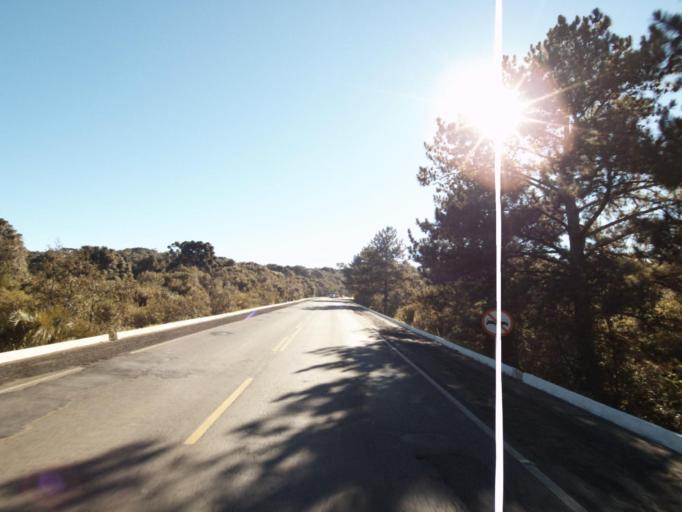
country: BR
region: Santa Catarina
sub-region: Concordia
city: Concordia
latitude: -26.9581
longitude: -51.8367
